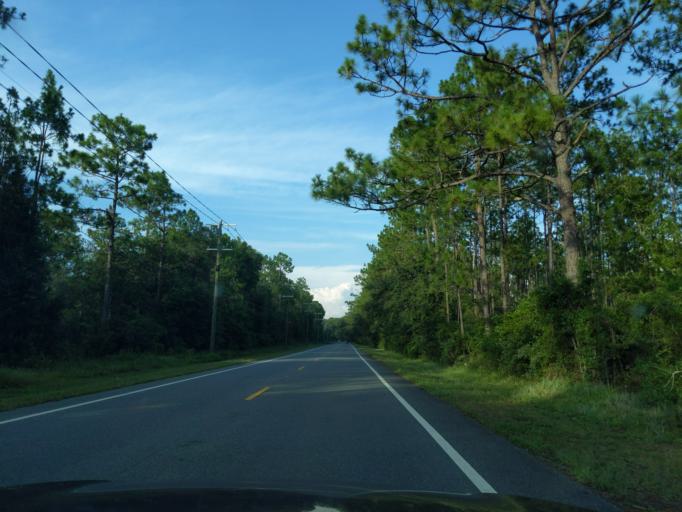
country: US
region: Florida
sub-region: Leon County
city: Tallahassee
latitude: 30.3846
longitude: -84.3366
